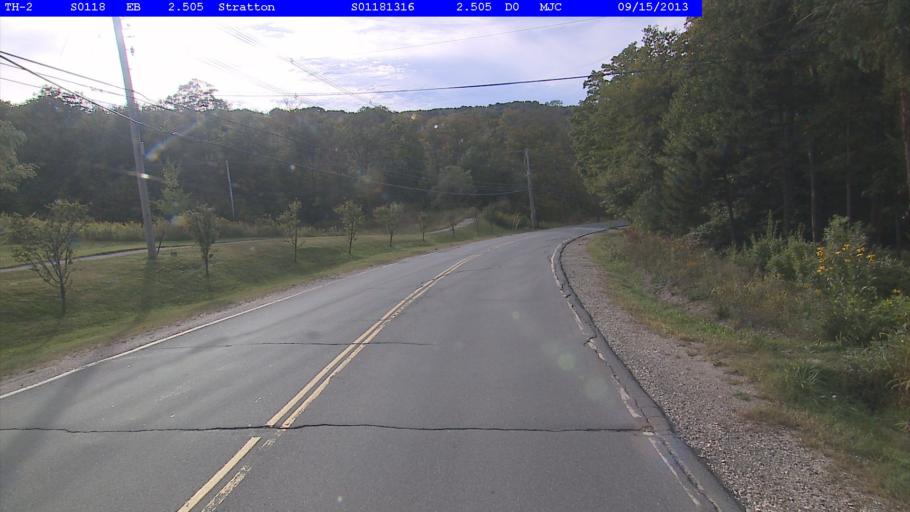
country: US
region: Vermont
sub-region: Bennington County
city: Manchester Center
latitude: 43.1150
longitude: -72.9079
